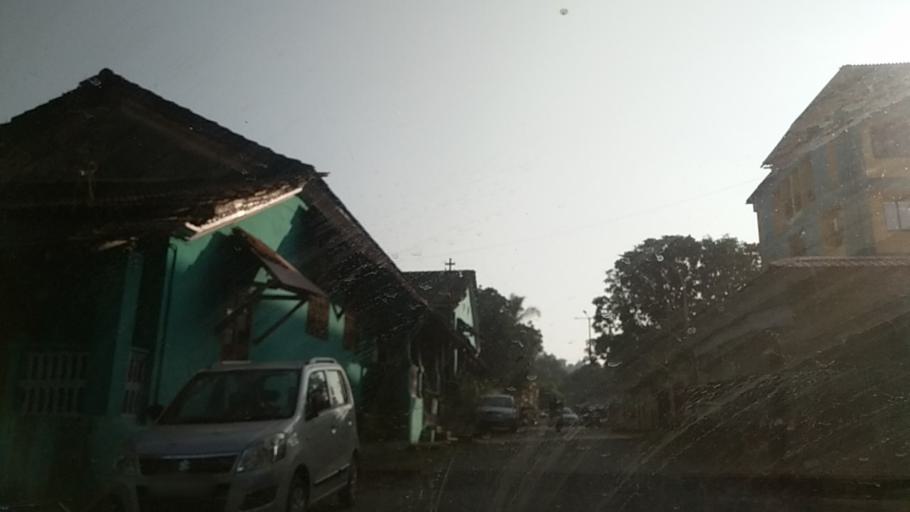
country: IN
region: Goa
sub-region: South Goa
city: Madgaon
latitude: 15.2790
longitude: 73.9556
